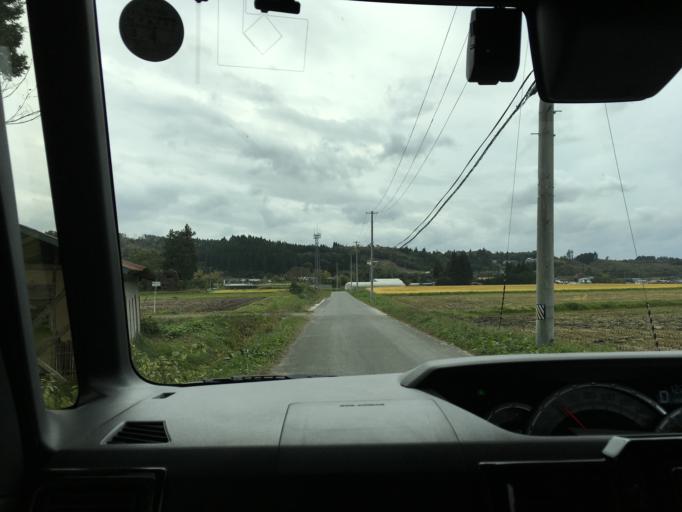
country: JP
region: Iwate
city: Ichinoseki
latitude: 39.0198
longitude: 141.3495
